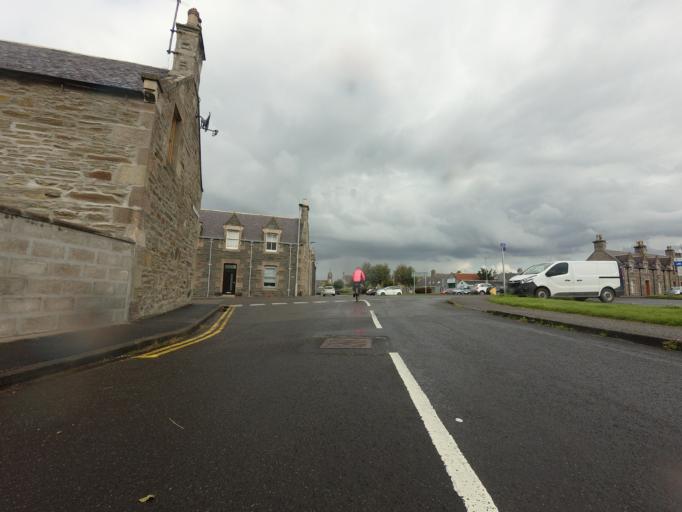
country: GB
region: Scotland
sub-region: Moray
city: Buckie
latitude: 57.6759
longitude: -2.9709
